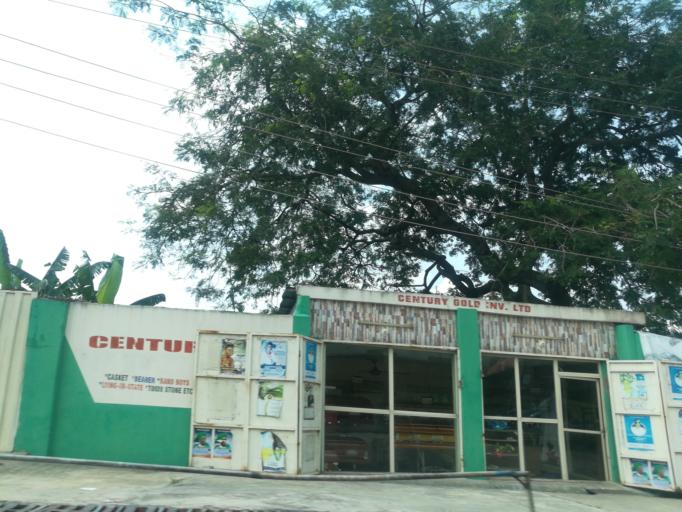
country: NG
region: Oyo
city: Ibadan
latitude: 7.3998
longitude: 3.8996
